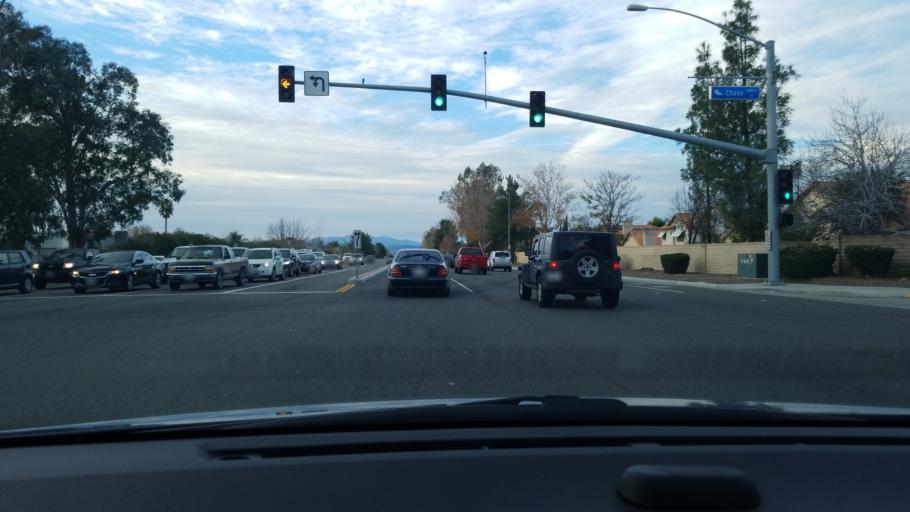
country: US
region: California
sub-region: Riverside County
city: San Jacinto
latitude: 33.8043
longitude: -116.9772
